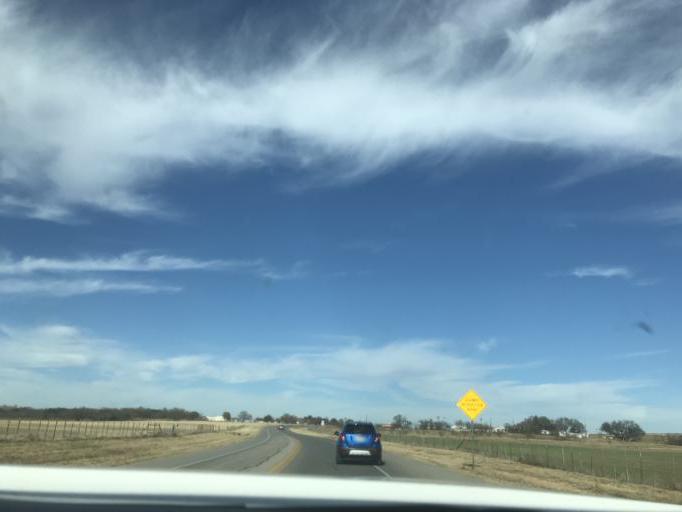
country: US
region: Texas
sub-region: Erath County
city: Stephenville
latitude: 32.2389
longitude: -98.1986
